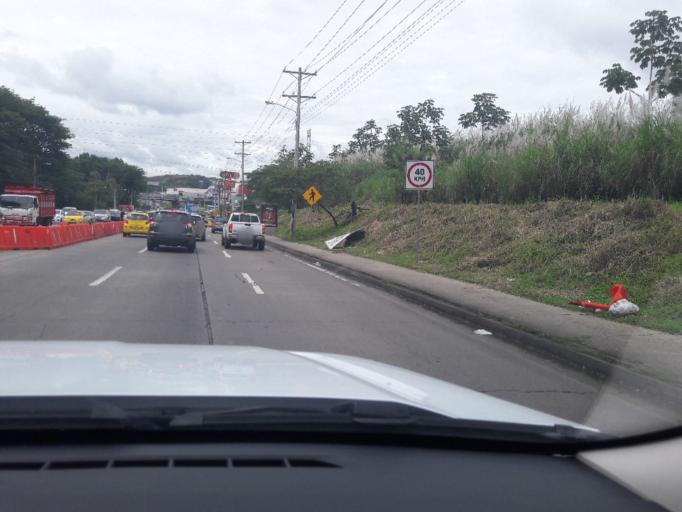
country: PA
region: Panama
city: Panama
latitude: 9.0259
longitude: -79.5288
